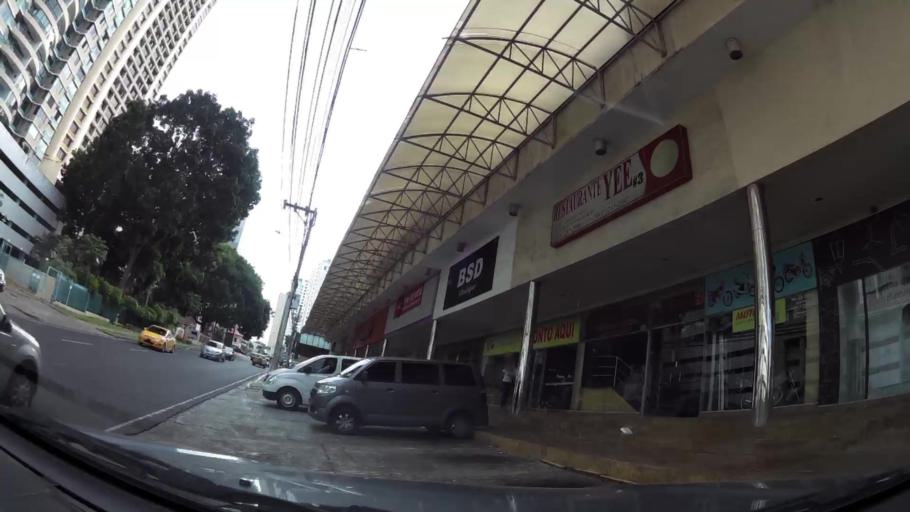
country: PA
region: Panama
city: Panama
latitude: 8.9780
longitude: -79.5156
